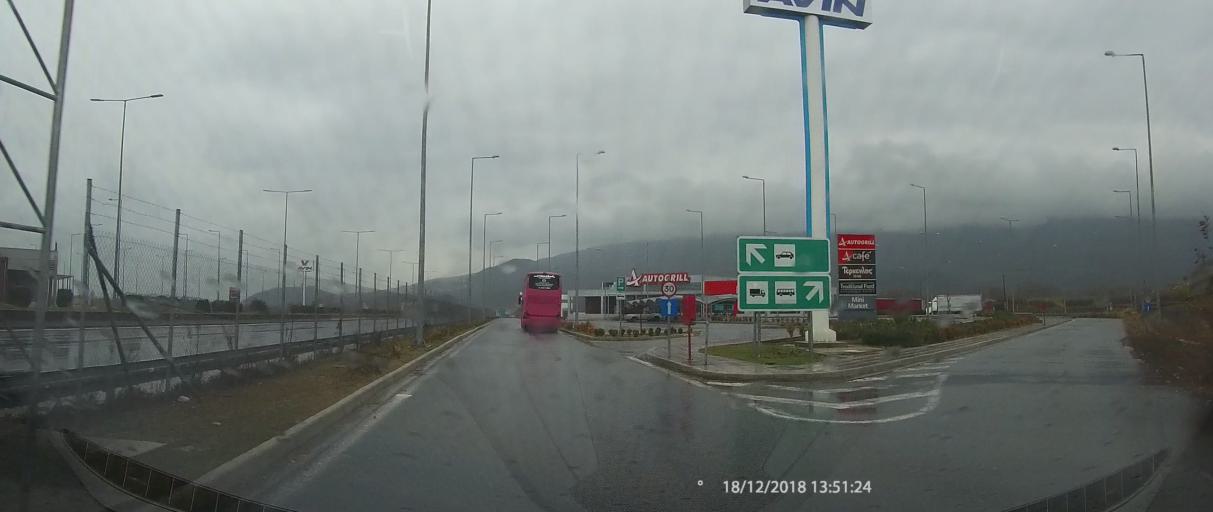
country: GR
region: Central Macedonia
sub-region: Nomos Pierias
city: Leptokarya
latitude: 40.0280
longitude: 22.5724
